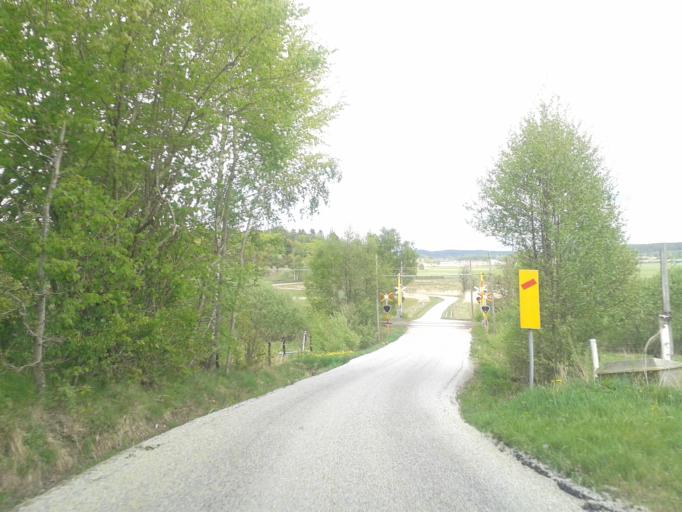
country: SE
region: Vaestra Goetaland
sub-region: Kungalvs Kommun
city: Kode
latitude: 57.8952
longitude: 11.9077
